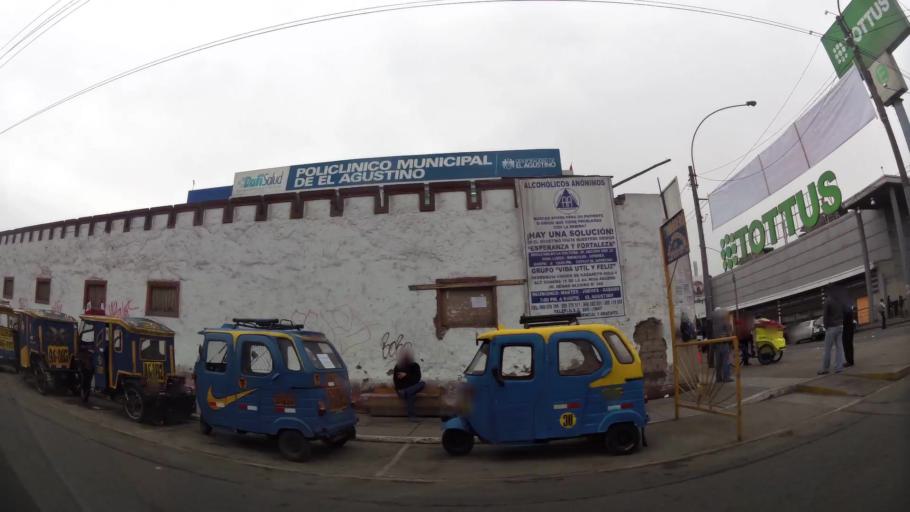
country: PE
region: Lima
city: Lima
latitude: -12.0409
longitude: -77.0009
